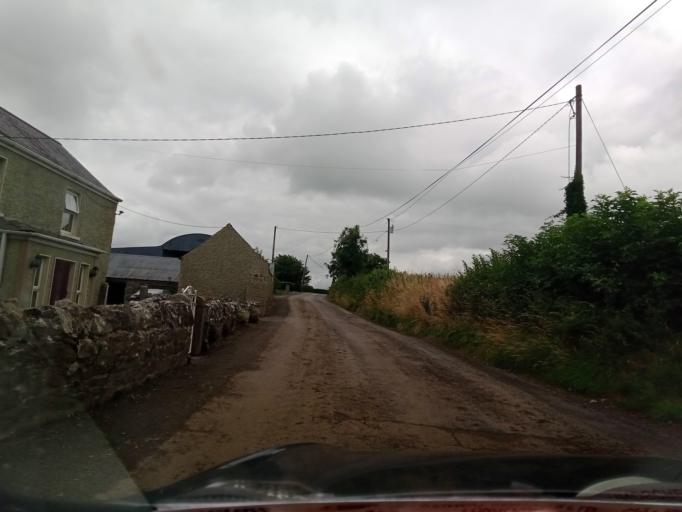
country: IE
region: Leinster
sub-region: Laois
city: Stradbally
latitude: 52.9608
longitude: -7.1854
